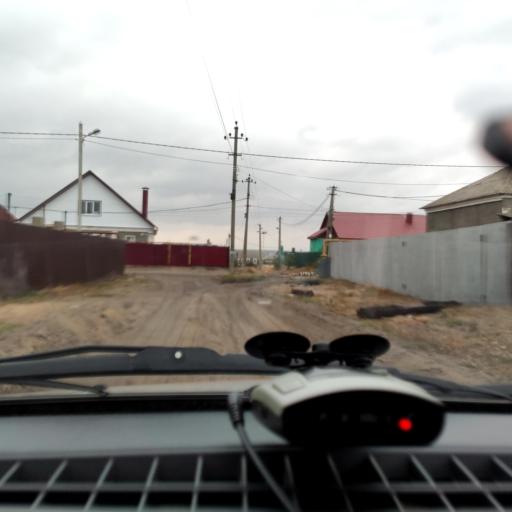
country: RU
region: Voronezj
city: Pridonskoy
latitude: 51.7050
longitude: 39.0686
